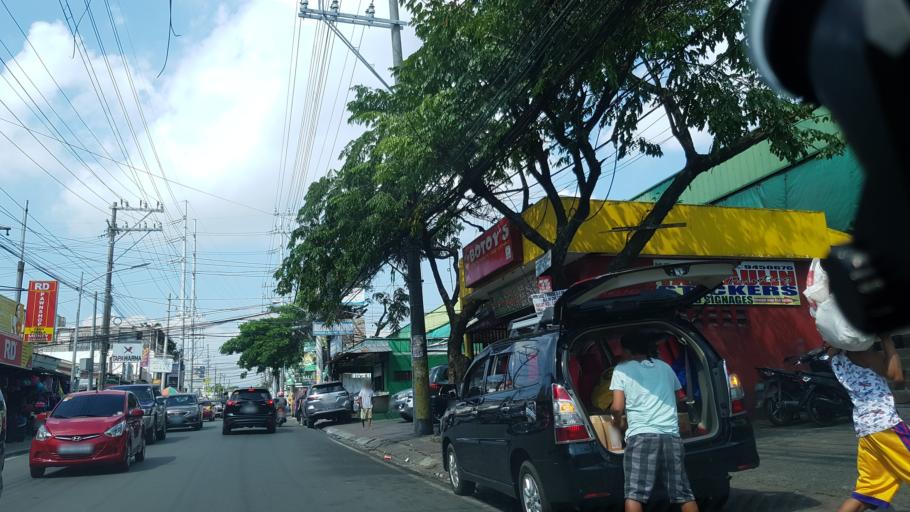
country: PH
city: Sambayanihan People's Village
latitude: 14.4658
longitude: 121.0201
